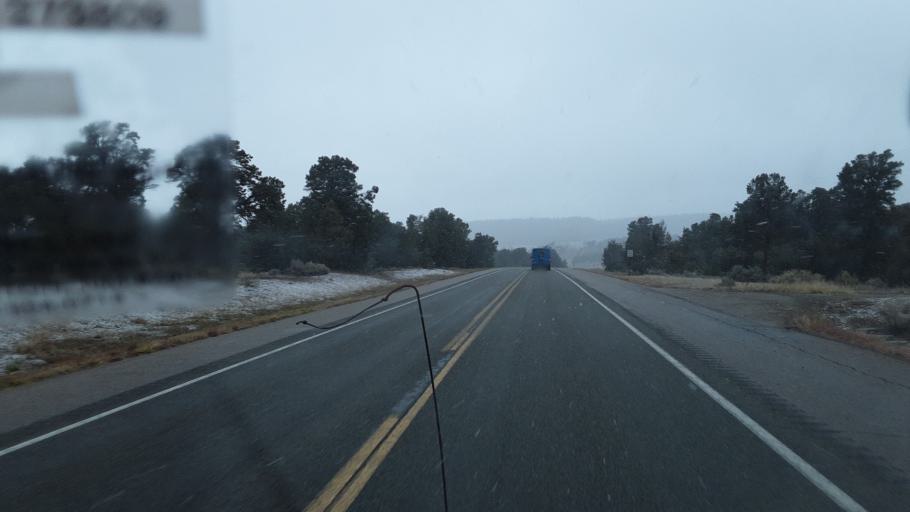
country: US
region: New Mexico
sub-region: Rio Arriba County
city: Tierra Amarilla
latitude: 36.4849
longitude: -106.4940
